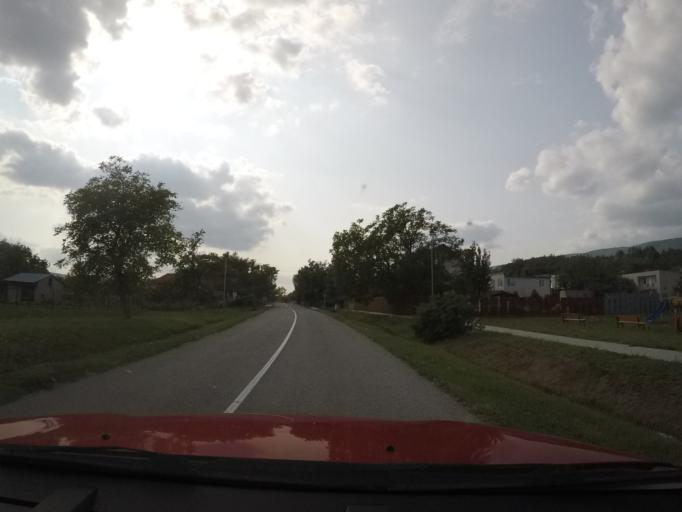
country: SK
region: Kosicky
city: Medzev
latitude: 48.6019
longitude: 20.8435
